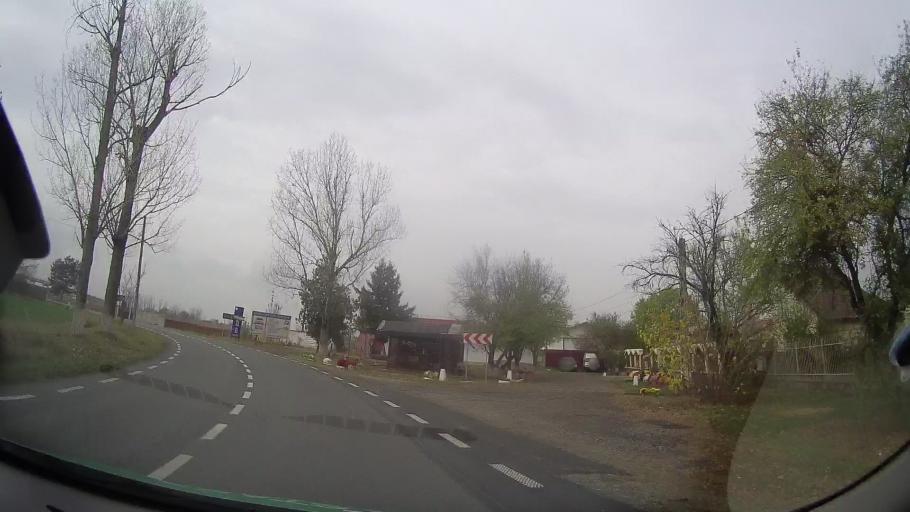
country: RO
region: Ilfov
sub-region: Comuna Gruiu
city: Lipia
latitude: 44.7177
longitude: 26.2484
